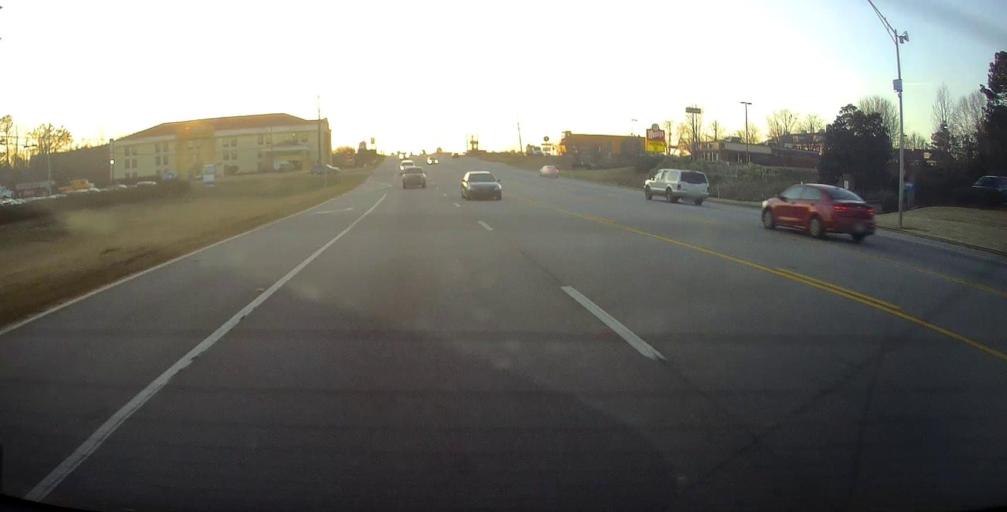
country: US
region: Georgia
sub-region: Troup County
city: La Grange
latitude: 33.0422
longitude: -84.9769
